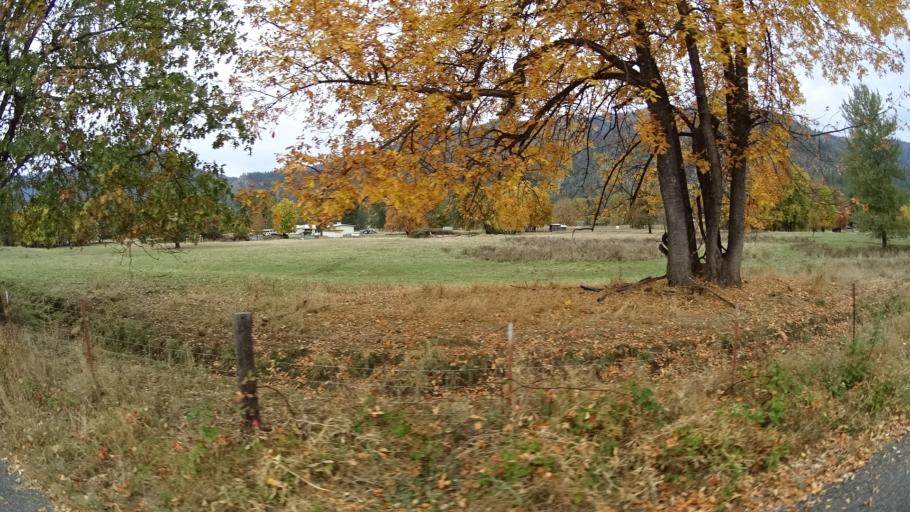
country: US
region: California
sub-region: Siskiyou County
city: Happy Camp
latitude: 41.8412
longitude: -123.1908
